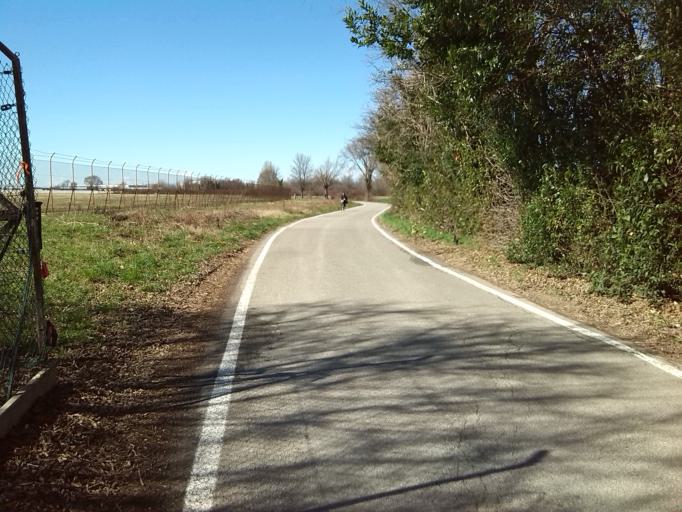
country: IT
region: Friuli Venezia Giulia
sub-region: Provincia di Gorizia
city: Ronchi dei Legionari
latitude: 45.8305
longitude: 13.4909
